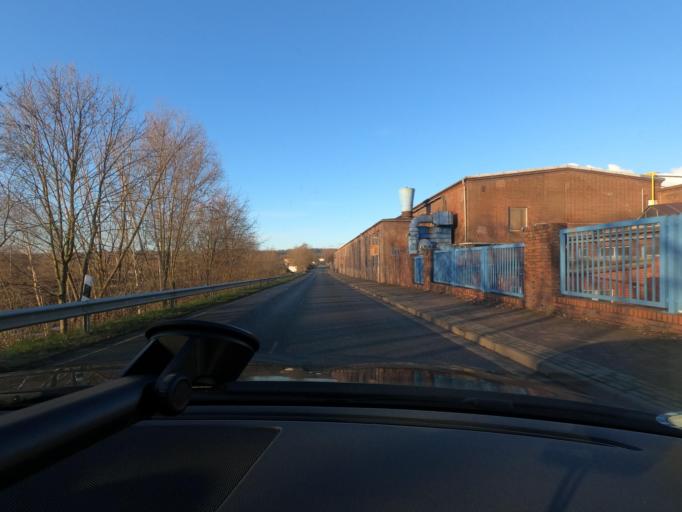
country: DE
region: Lower Saxony
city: Herzberg am Harz
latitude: 51.6403
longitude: 10.3329
